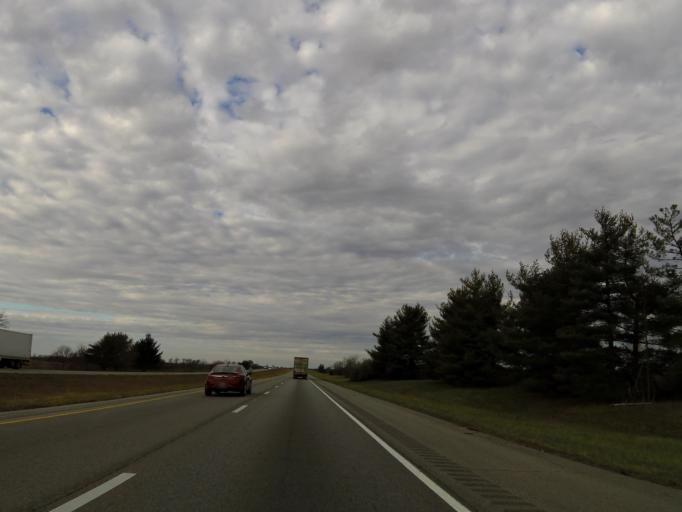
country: US
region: Illinois
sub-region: Jefferson County
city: Mount Vernon
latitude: 38.3623
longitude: -89.0620
